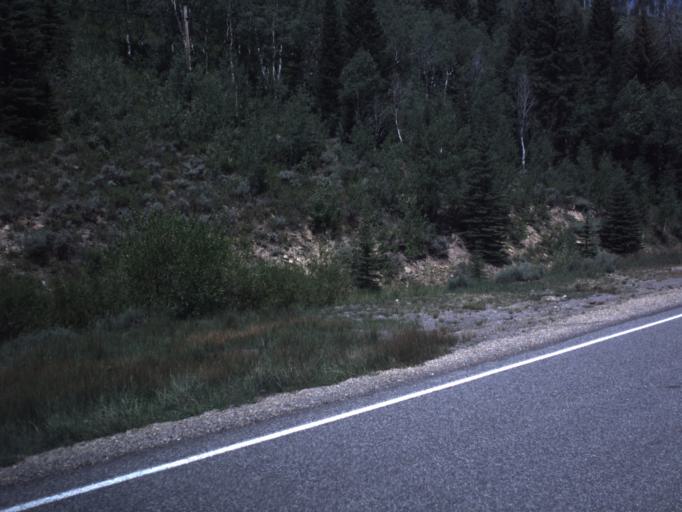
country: US
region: Utah
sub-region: Sanpete County
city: Fairview
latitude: 39.6624
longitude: -111.1557
